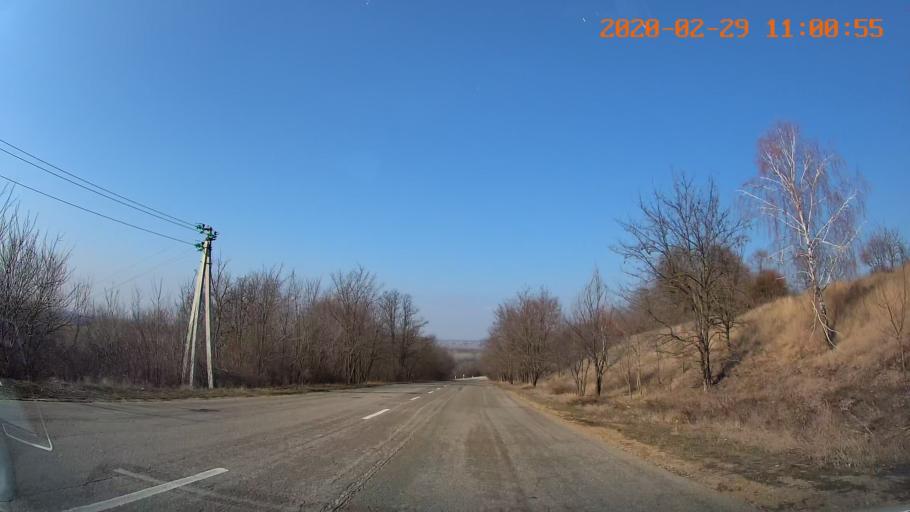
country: MD
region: Telenesti
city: Grigoriopol
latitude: 47.1610
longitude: 29.2683
